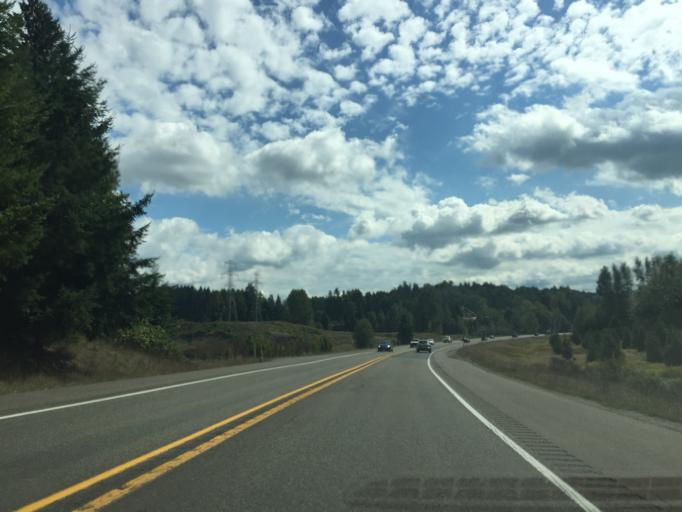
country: US
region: Washington
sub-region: Snohomish County
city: Snohomish
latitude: 47.9416
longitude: -122.0715
